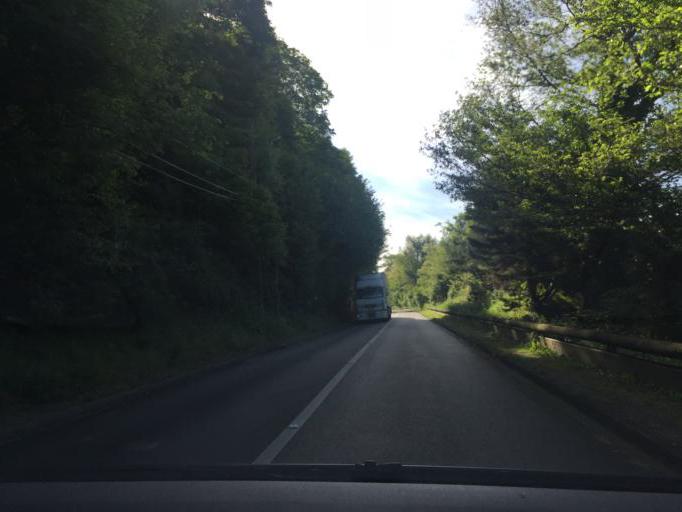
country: FR
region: Ile-de-France
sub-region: Departement des Yvelines
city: Chateaufort
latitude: 48.7329
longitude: 2.0962
